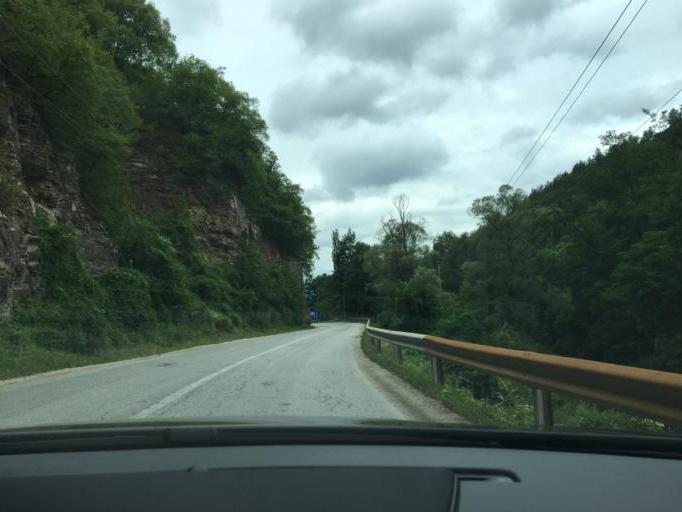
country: MK
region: Kriva Palanka
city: Kriva Palanka
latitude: 42.2164
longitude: 22.3512
